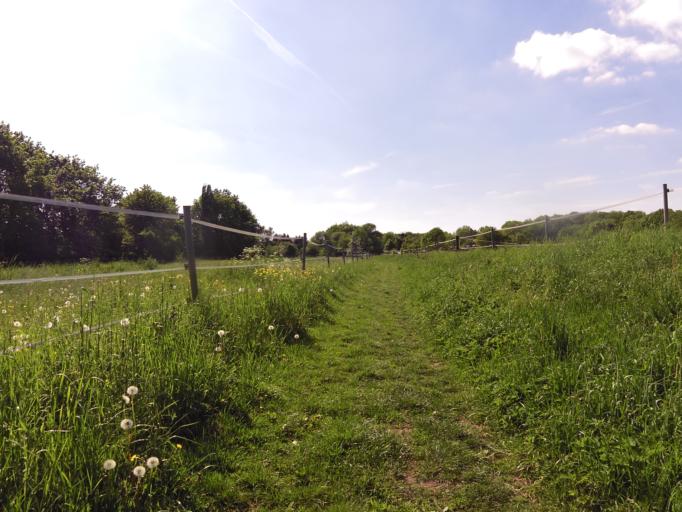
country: DE
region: Saxony
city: Markkleeberg
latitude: 51.3004
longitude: 12.3382
